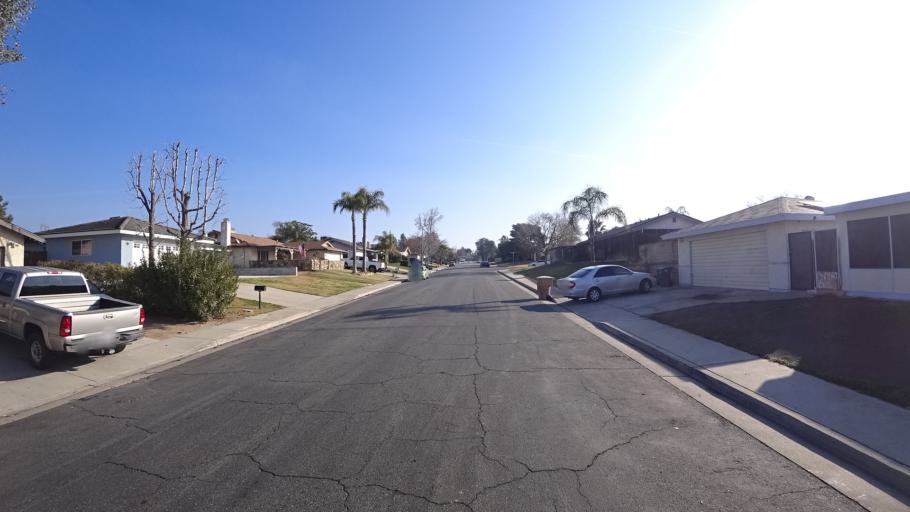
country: US
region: California
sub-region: Kern County
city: Oildale
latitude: 35.4019
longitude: -118.9286
